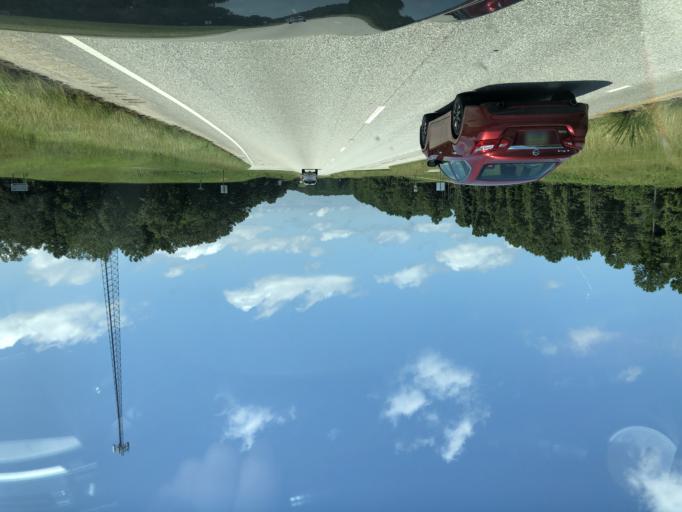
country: US
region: Alabama
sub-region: Henry County
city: Abbeville
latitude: 31.7412
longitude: -85.2453
